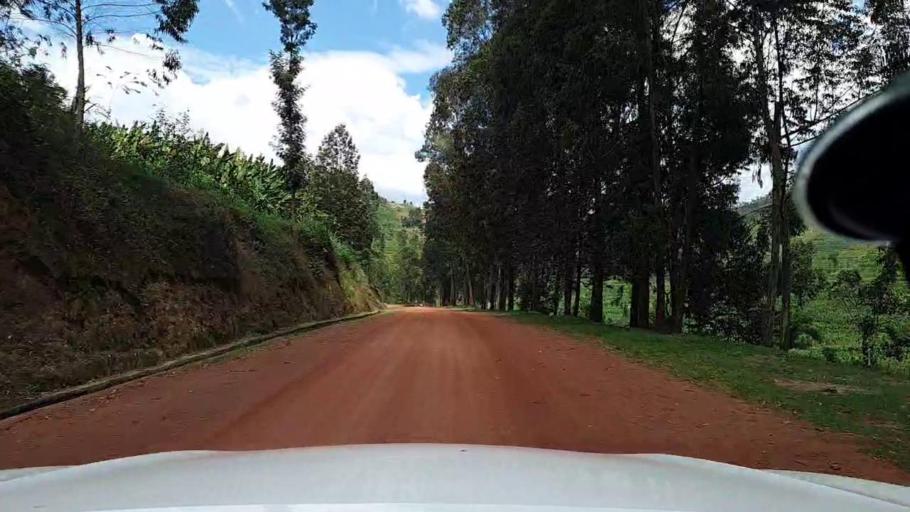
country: RW
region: Northern Province
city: Byumba
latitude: -1.7062
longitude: 29.8485
